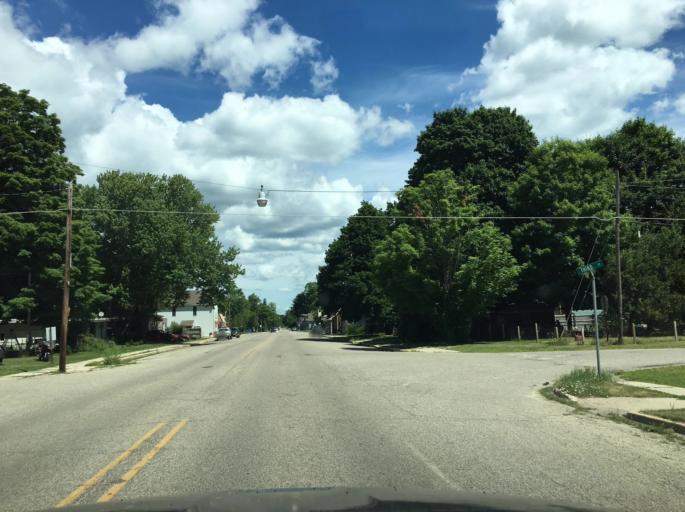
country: US
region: Michigan
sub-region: Osceola County
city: Reed City
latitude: 43.8485
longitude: -85.4444
